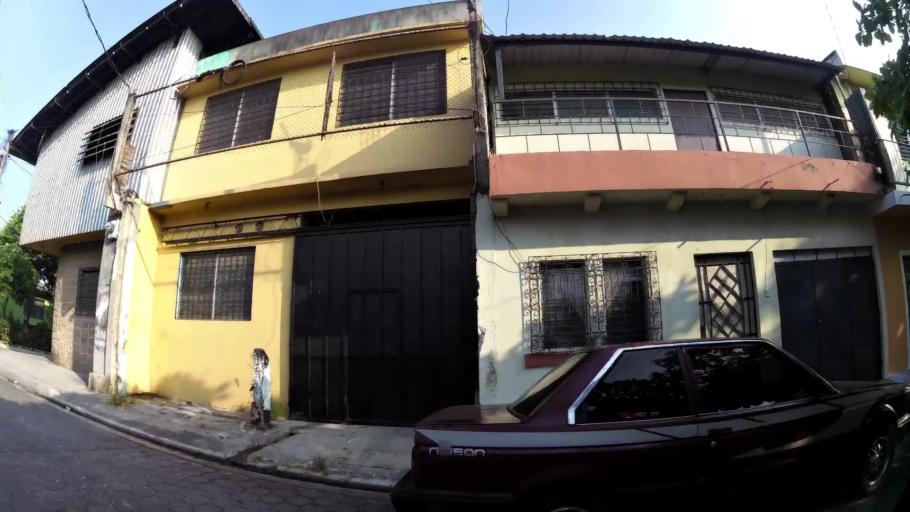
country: SV
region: San Salvador
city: San Salvador
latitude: 13.6885
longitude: -89.2049
